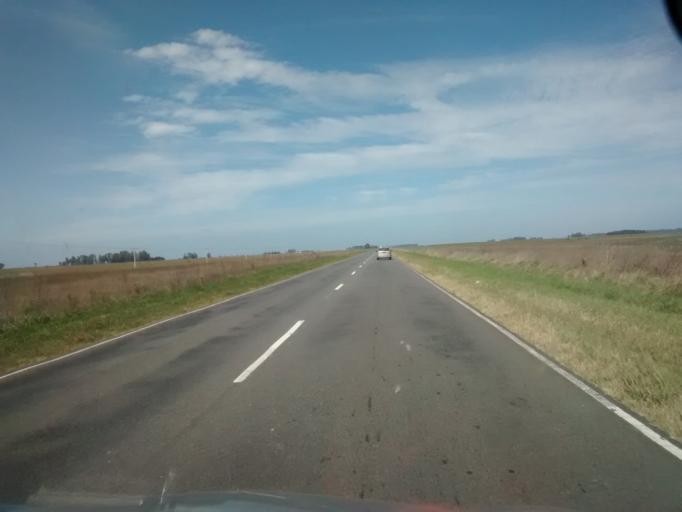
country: AR
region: Buenos Aires
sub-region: Partido de Ayacucho
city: Ayacucho
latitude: -36.6631
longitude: -58.5743
